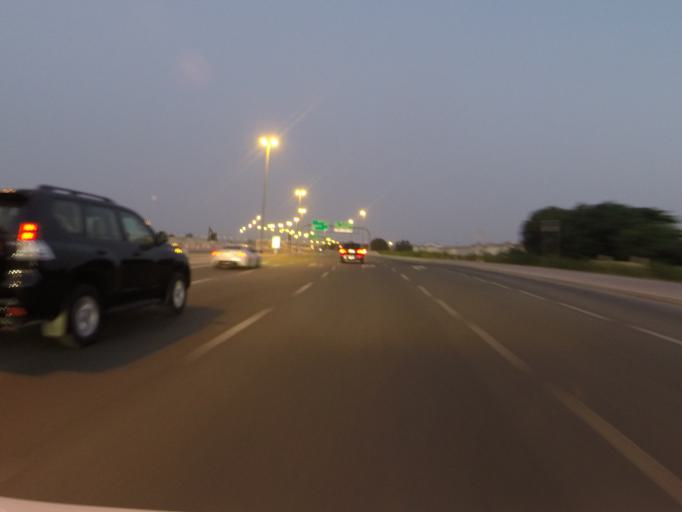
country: AE
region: Dubai
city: Dubai
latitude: 25.0811
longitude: 55.1744
